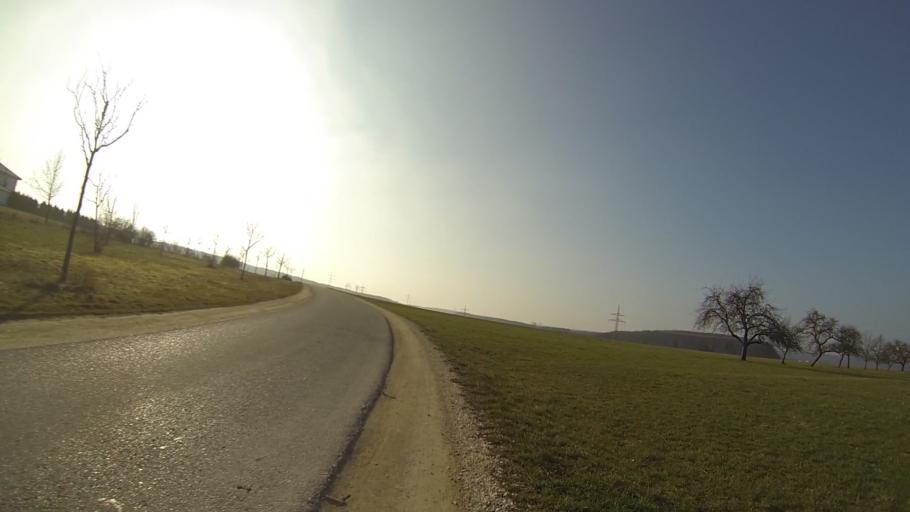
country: DE
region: Baden-Wuerttemberg
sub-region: Regierungsbezirk Stuttgart
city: Nattheim
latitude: 48.7383
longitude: 10.2411
